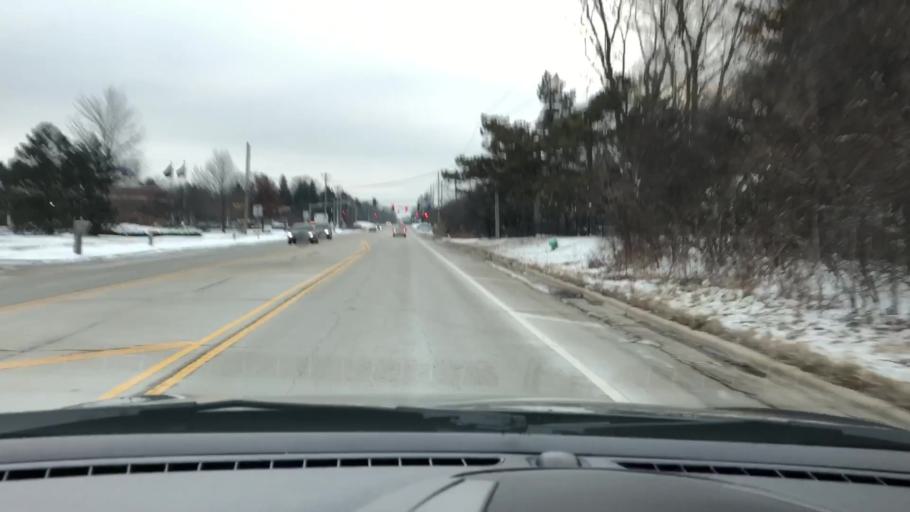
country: US
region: Illinois
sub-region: Cook County
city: Lemont
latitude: 41.6661
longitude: -87.9599
